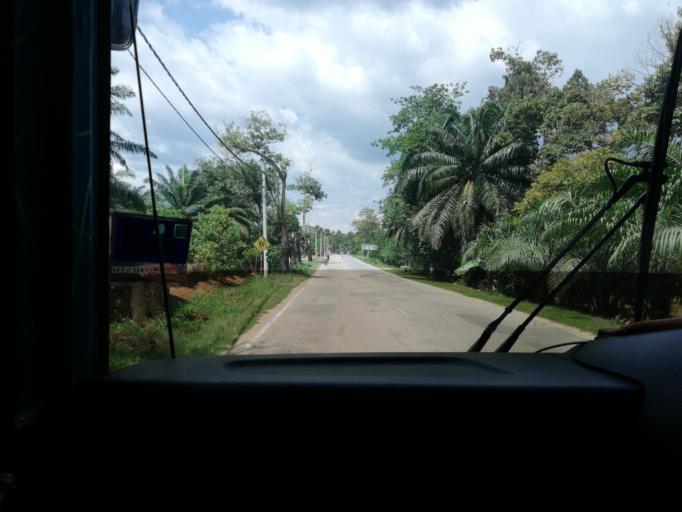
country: MY
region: Perak
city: Parit Buntar
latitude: 5.1148
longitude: 100.5580
